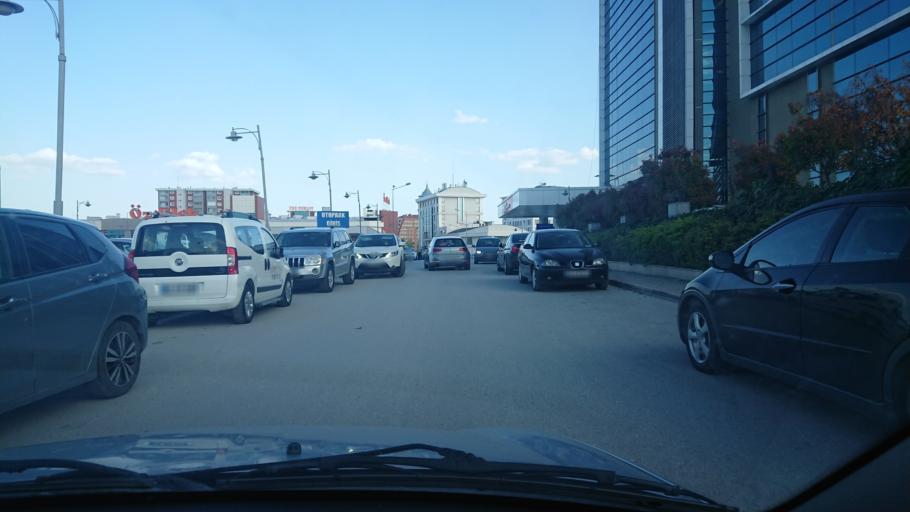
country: TR
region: Eskisehir
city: Eskisehir
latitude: 39.7854
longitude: 30.4952
